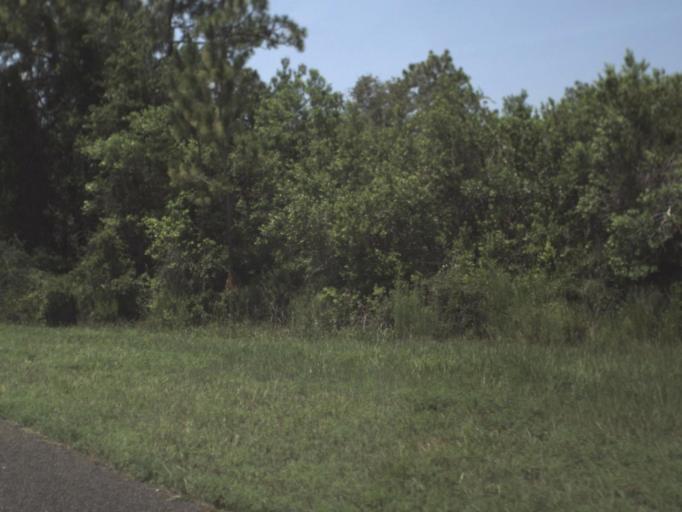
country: US
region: Florida
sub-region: Citrus County
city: Sugarmill Woods
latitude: 28.6980
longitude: -82.5527
